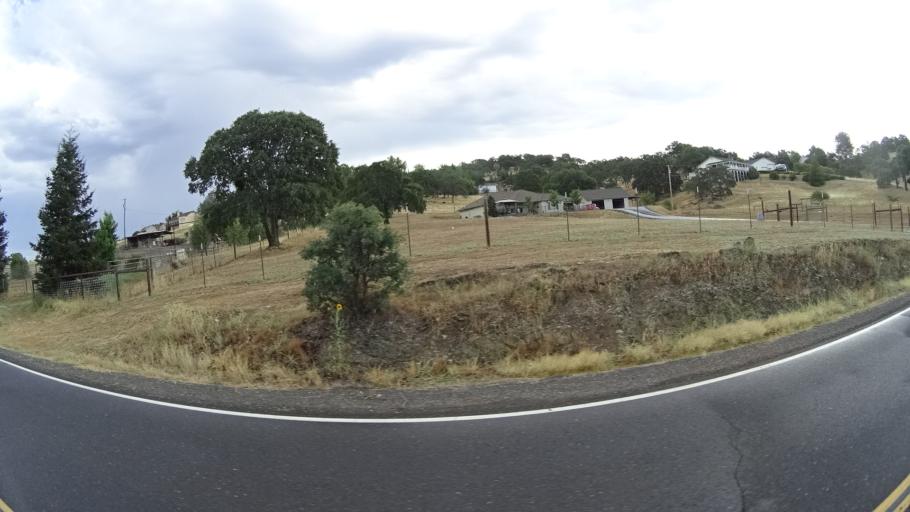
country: US
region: California
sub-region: Calaveras County
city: Copperopolis
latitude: 37.9259
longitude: -120.6370
